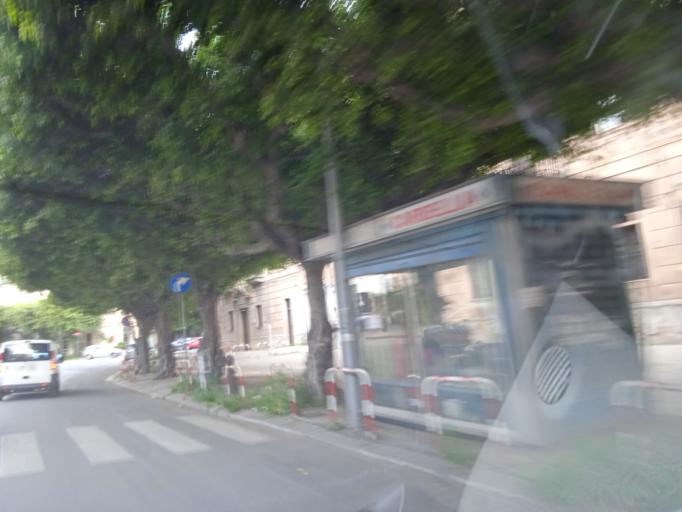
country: IT
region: Sicily
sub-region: Palermo
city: Palermo
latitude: 38.1215
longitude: 13.3527
